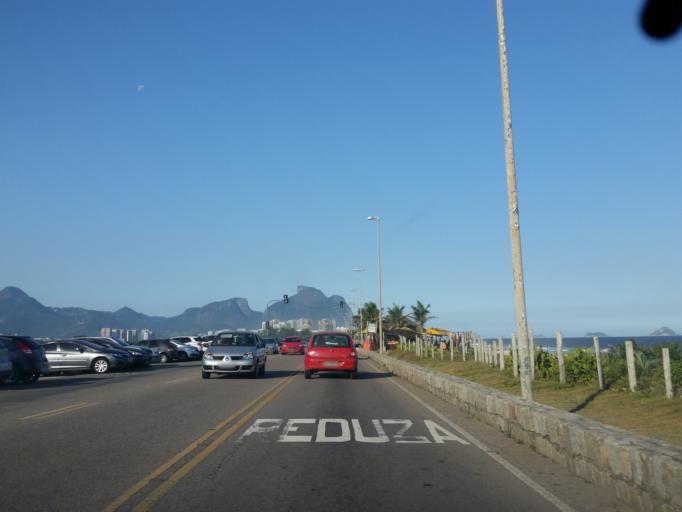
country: BR
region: Rio de Janeiro
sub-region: Nilopolis
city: Nilopolis
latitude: -23.0129
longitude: -43.3917
